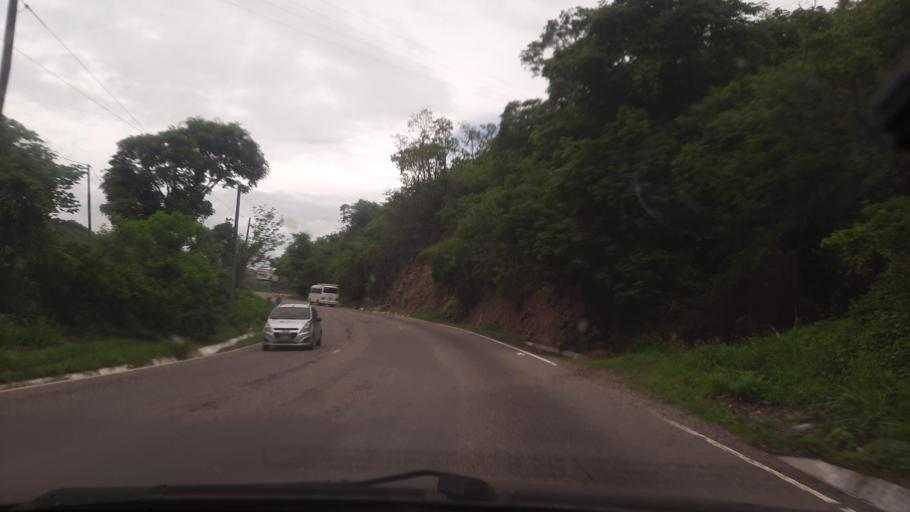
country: GT
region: Chiquimula
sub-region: Municipio de Chiquimula
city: Chiquimula
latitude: 14.8749
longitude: -89.5123
